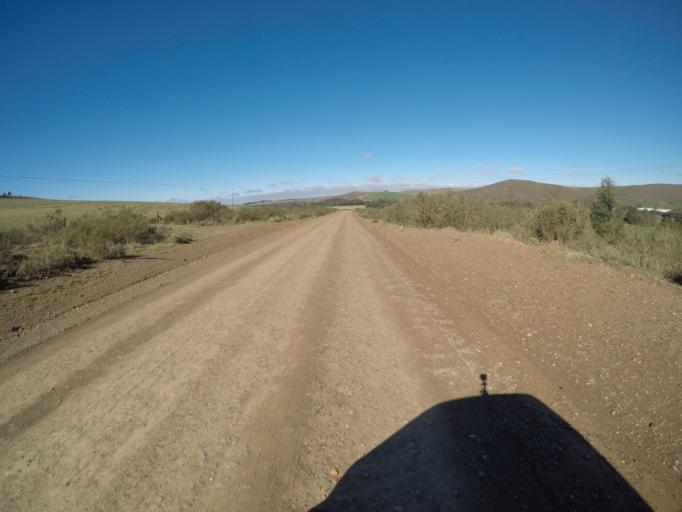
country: ZA
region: Western Cape
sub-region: Overberg District Municipality
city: Caledon
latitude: -34.0808
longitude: 19.6459
